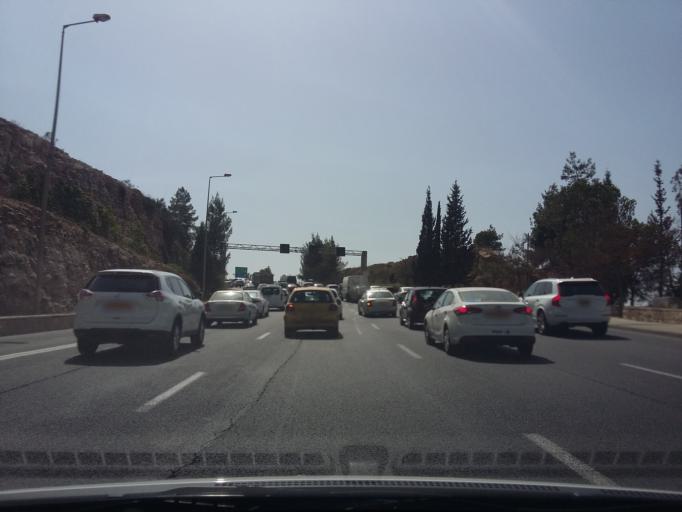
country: IL
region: Jerusalem
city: West Jerusalem
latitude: 31.7988
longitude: 35.2007
